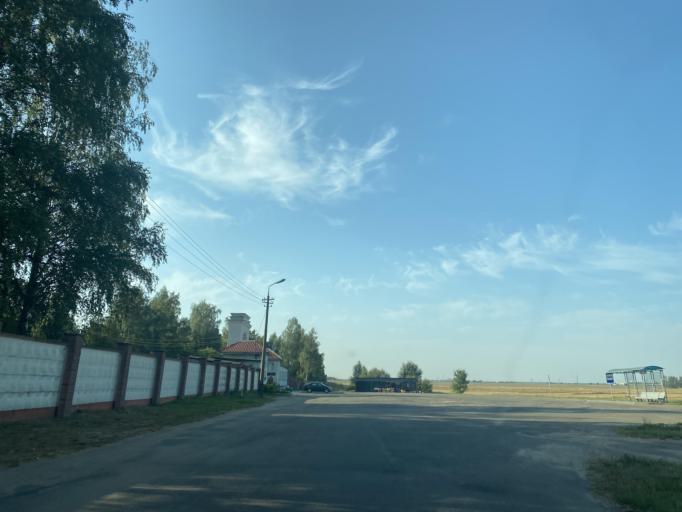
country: BY
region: Minsk
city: Hatava
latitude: 53.8282
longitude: 27.6381
